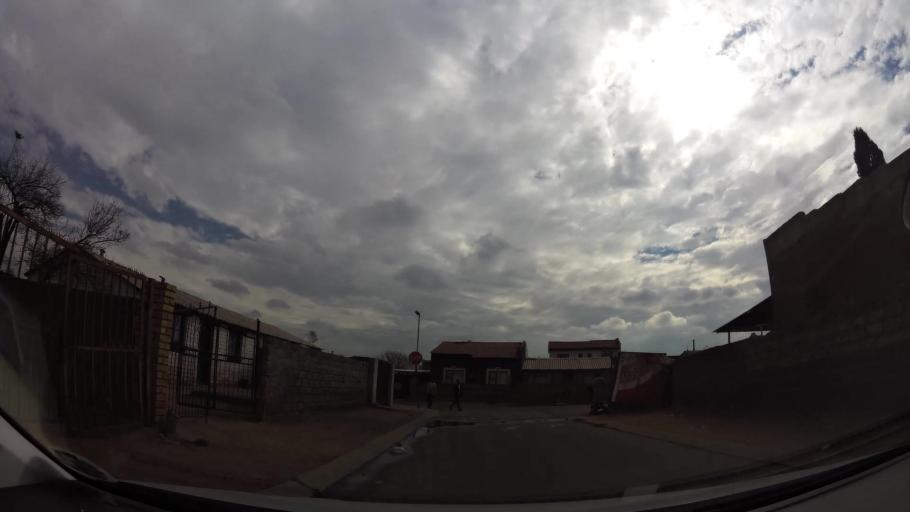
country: ZA
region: Gauteng
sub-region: City of Johannesburg Metropolitan Municipality
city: Soweto
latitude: -26.2684
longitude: 27.8534
